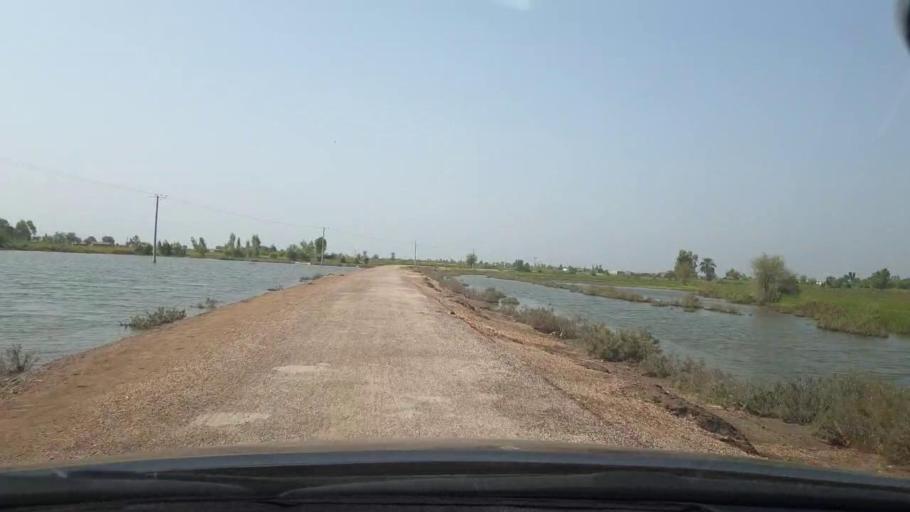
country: PK
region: Sindh
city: Tando Bago
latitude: 24.7125
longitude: 69.0884
